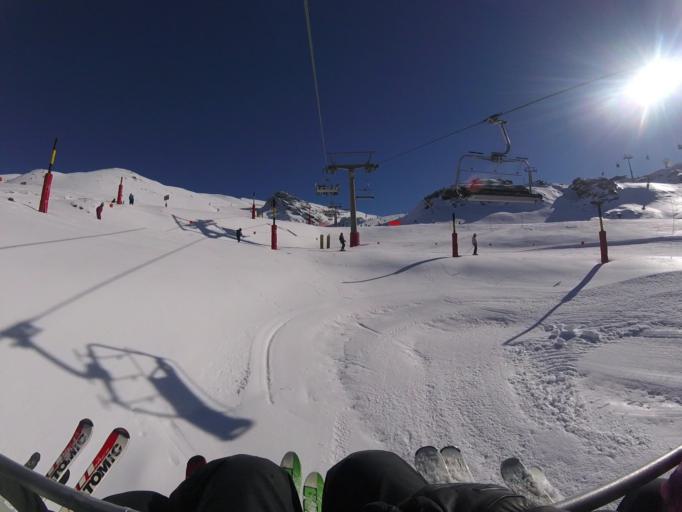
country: ES
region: Andalusia
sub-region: Provincia de Granada
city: Guejar-Sierra
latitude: 37.0764
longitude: -3.3888
